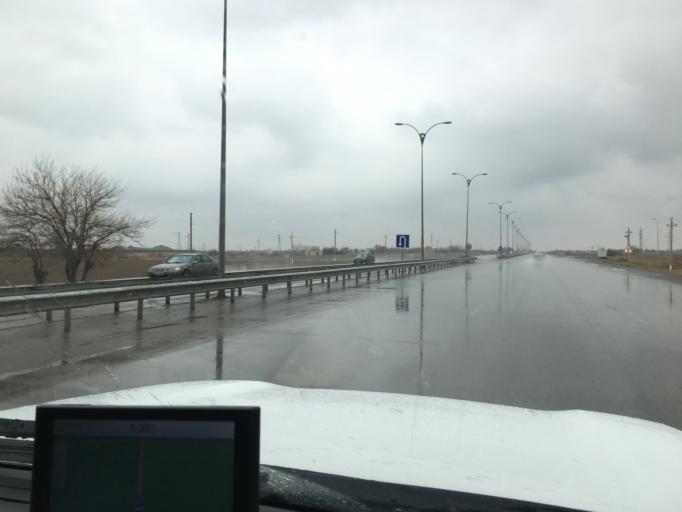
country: TM
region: Mary
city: Mary
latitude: 37.5409
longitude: 61.8774
